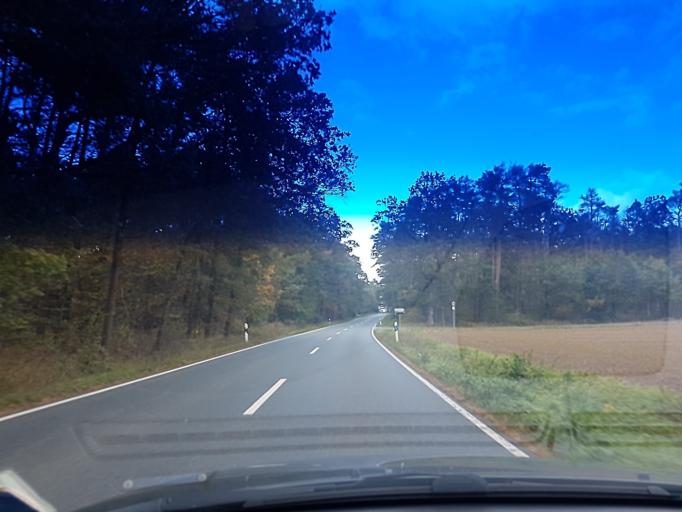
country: DE
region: Bavaria
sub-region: Regierungsbezirk Mittelfranken
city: Hochstadt an der Aisch
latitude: 49.7223
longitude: 10.8178
